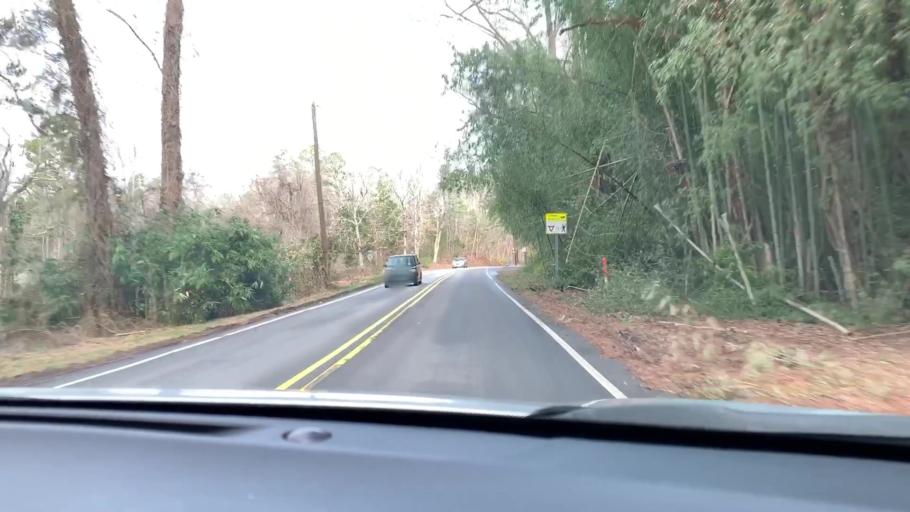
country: US
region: North Carolina
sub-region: Durham County
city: Durham
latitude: 35.9837
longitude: -78.9416
